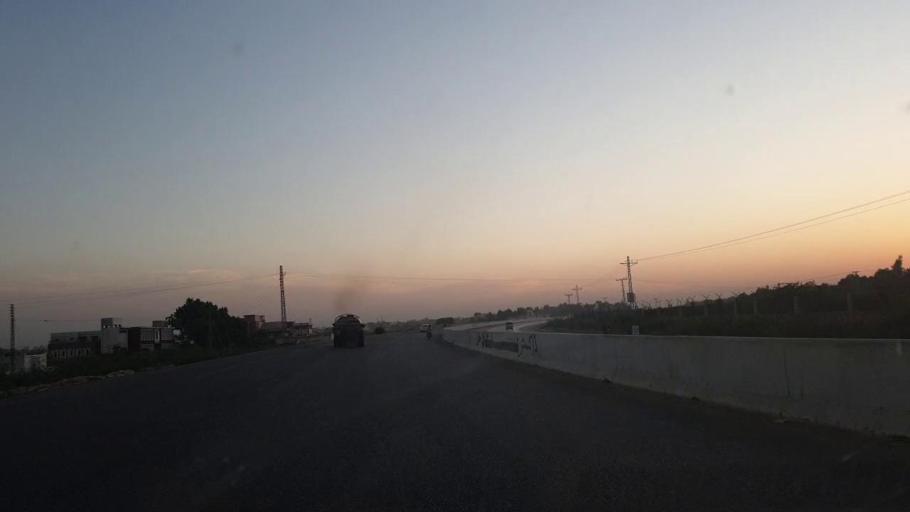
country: PK
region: Sindh
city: Jamshoro
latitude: 25.4214
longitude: 68.2803
